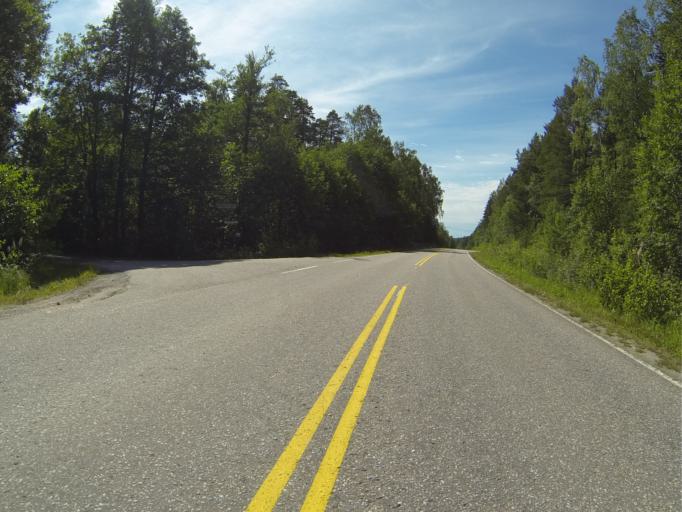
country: FI
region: Varsinais-Suomi
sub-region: Salo
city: Saerkisalo
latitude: 60.2640
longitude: 22.9733
